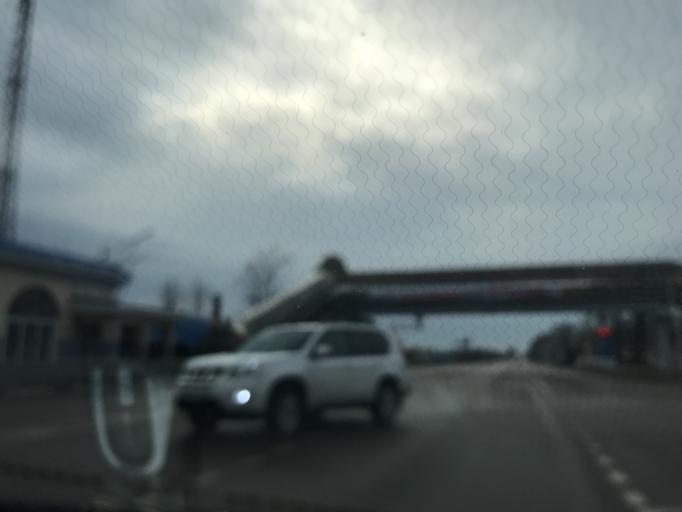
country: RU
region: Krasnodarskiy
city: Tikhoretsk
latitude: 45.8696
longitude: 40.1465
